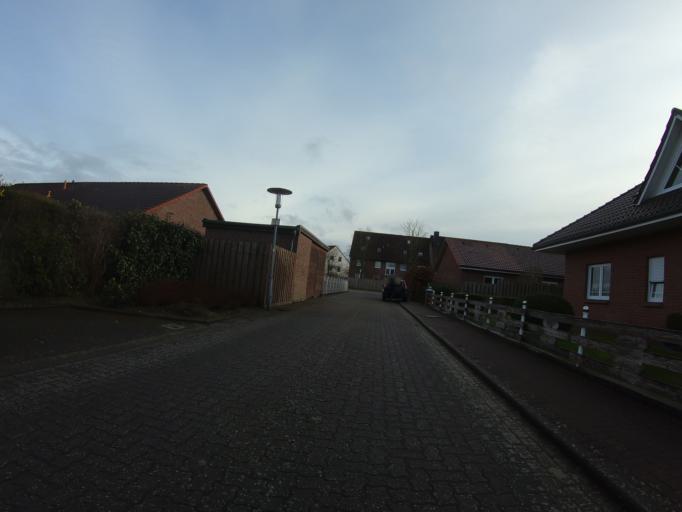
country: DE
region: Lower Saxony
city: Wesendorf
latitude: 52.6002
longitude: 10.5409
